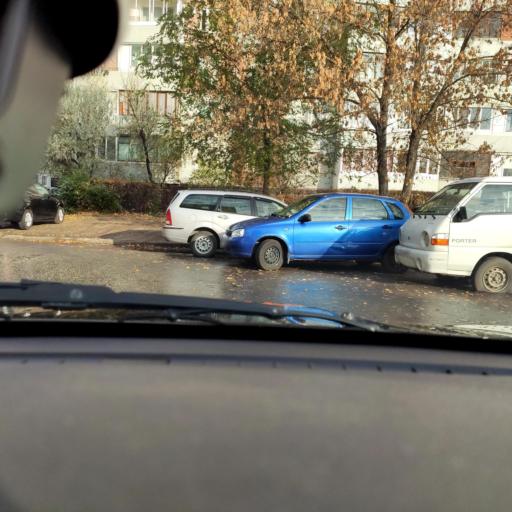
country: RU
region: Samara
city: Tol'yatti
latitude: 53.5400
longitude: 49.3212
